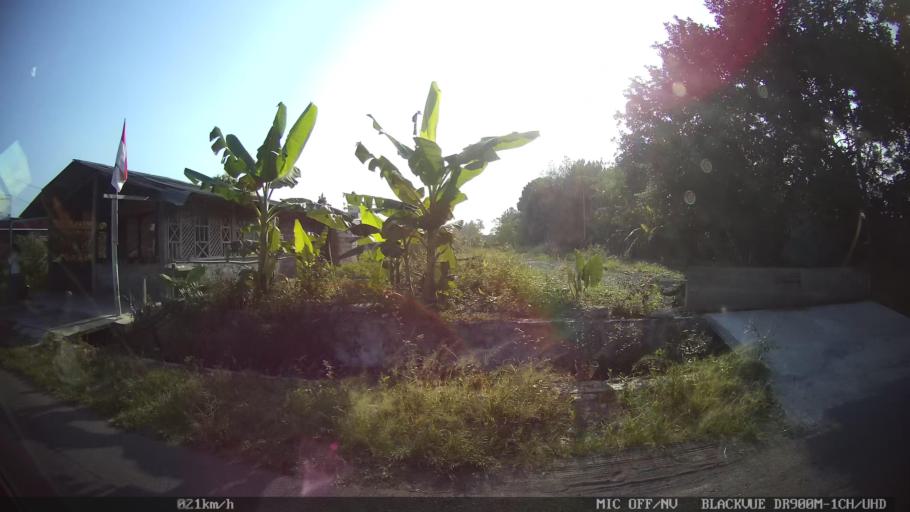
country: ID
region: Daerah Istimewa Yogyakarta
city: Gamping Lor
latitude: -7.7899
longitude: 110.3336
